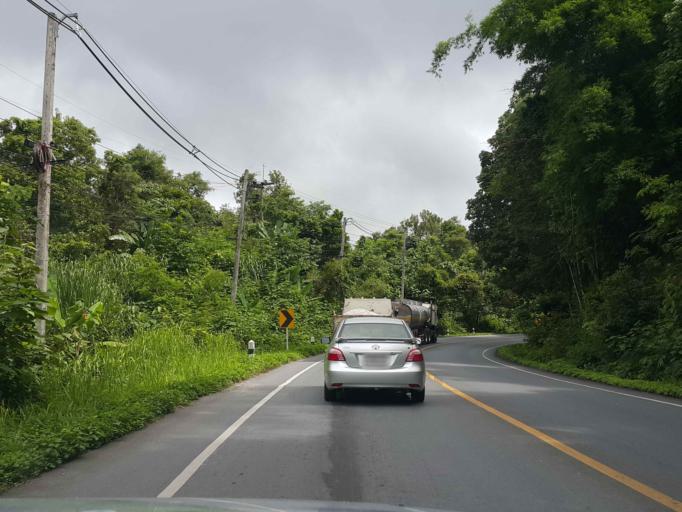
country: TH
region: Tak
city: Tak
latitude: 16.7957
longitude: 98.9512
